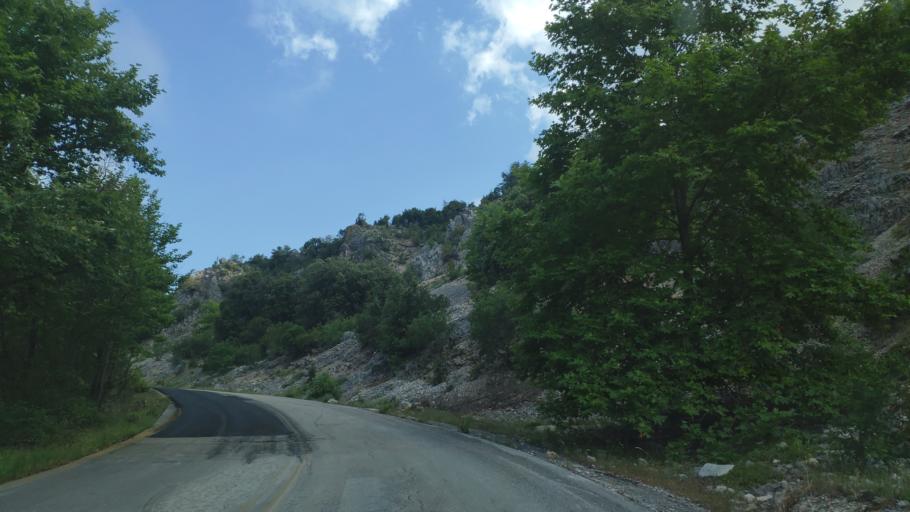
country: GR
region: Epirus
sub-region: Nomos Artas
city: Agios Dimitrios
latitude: 39.3973
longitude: 21.0177
